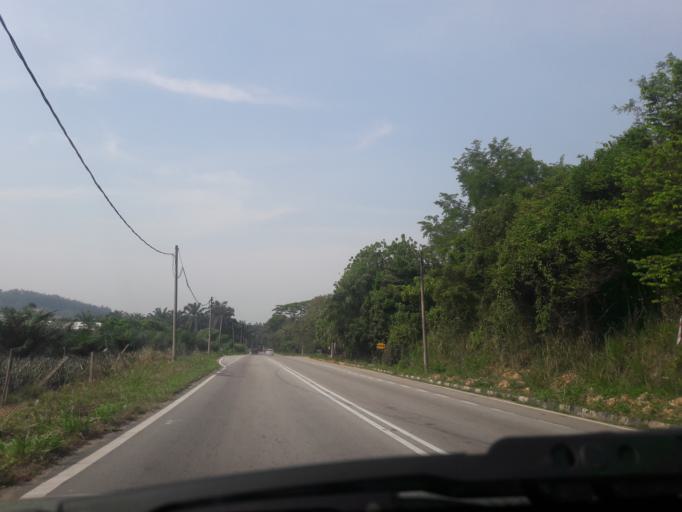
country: MY
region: Kedah
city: Kulim
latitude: 5.3512
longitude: 100.5200
